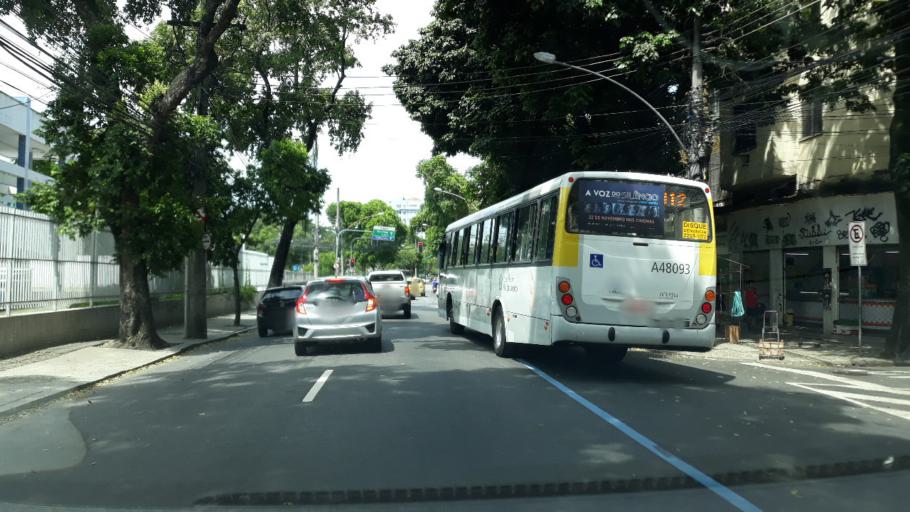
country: BR
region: Rio de Janeiro
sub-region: Rio De Janeiro
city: Rio de Janeiro
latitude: -22.9152
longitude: -43.2076
